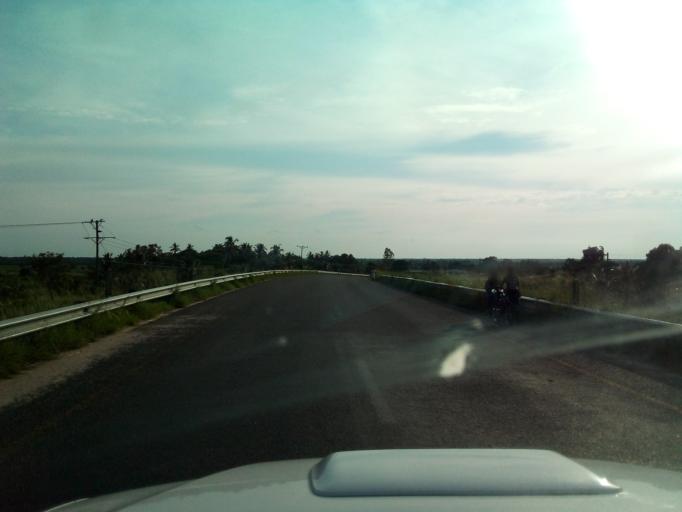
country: MZ
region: Zambezia
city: Quelimane
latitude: -17.4934
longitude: 37.0239
